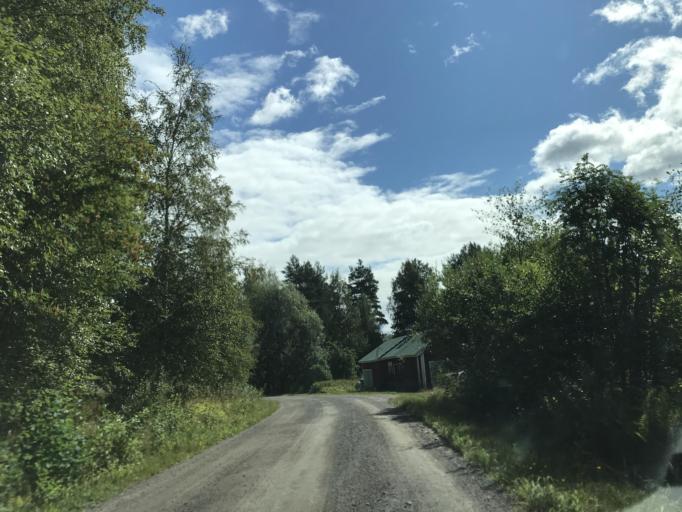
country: FI
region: Uusimaa
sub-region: Helsinki
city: Kaerkoelae
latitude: 60.6293
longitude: 23.8427
